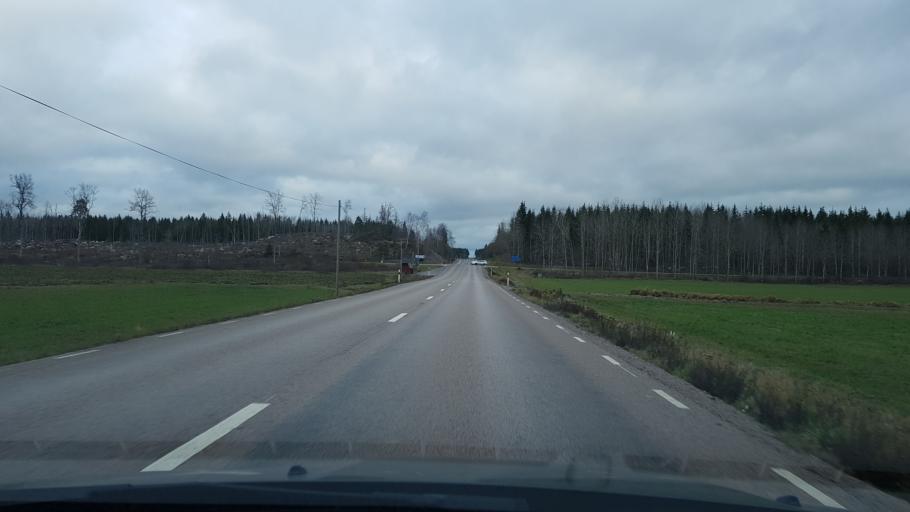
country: SE
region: Stockholm
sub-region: Norrtalje Kommun
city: Nykvarn
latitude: 59.9895
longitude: 18.2651
